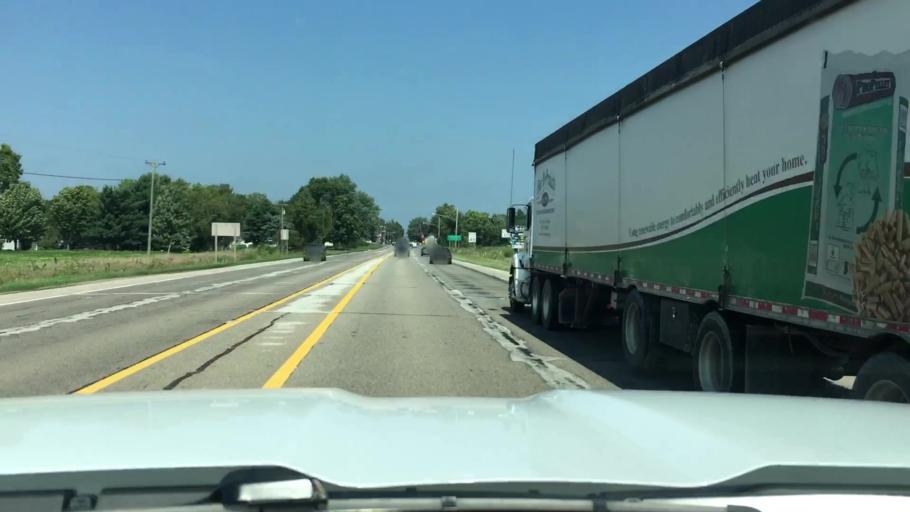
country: US
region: Michigan
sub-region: Kalamazoo County
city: Schoolcraft
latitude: 42.1056
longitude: -85.6370
